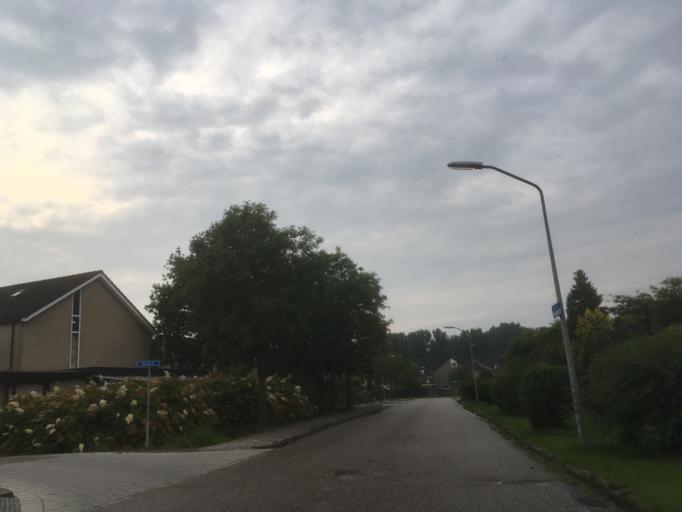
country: NL
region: Flevoland
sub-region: Gemeente Lelystad
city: Lelystad
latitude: 52.5231
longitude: 5.4680
